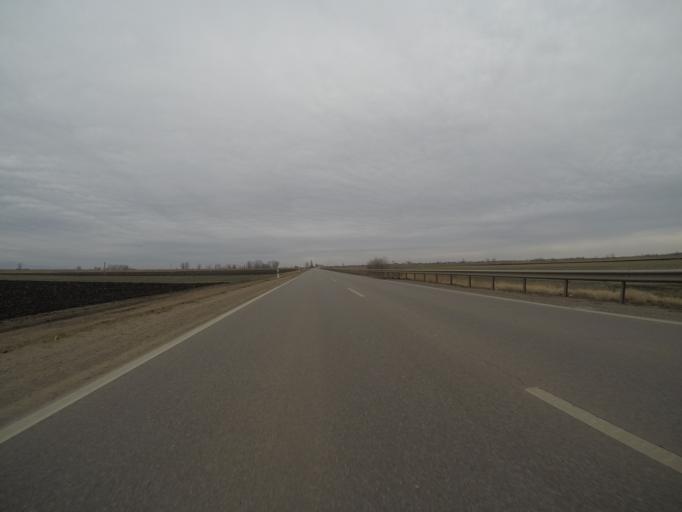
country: HU
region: Jasz-Nagykun-Szolnok
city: Jaszjakohalma
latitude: 47.5174
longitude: 19.9583
